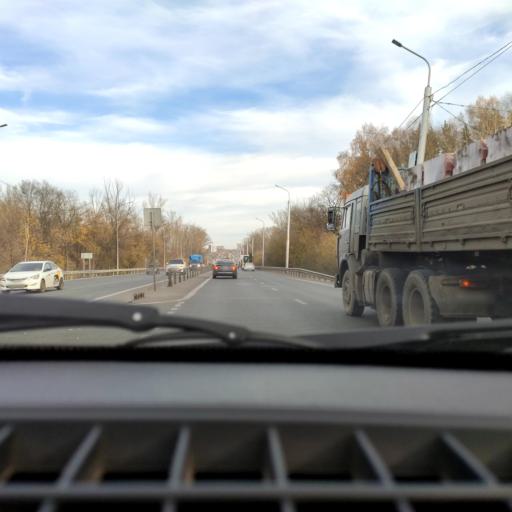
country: RU
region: Bashkortostan
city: Ufa
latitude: 54.7007
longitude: 55.9302
